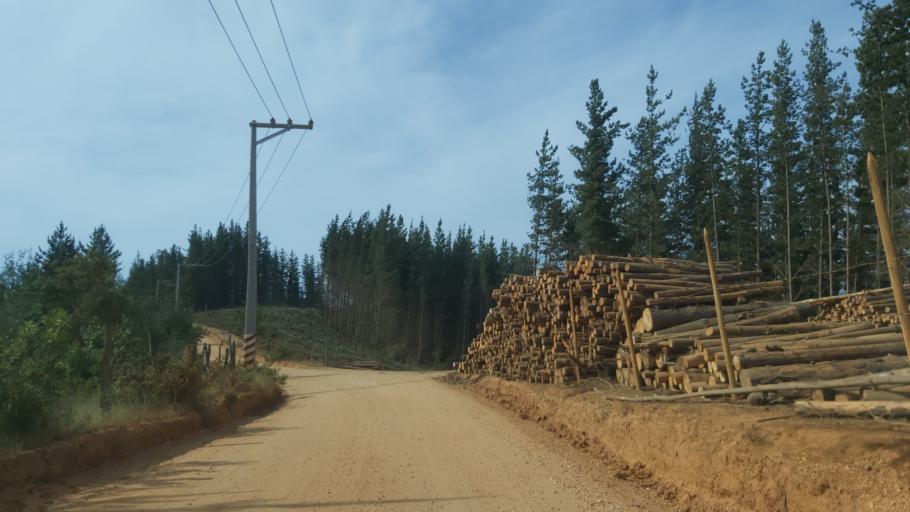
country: CL
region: Maule
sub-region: Provincia de Talca
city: Constitucion
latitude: -34.8511
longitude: -72.0333
